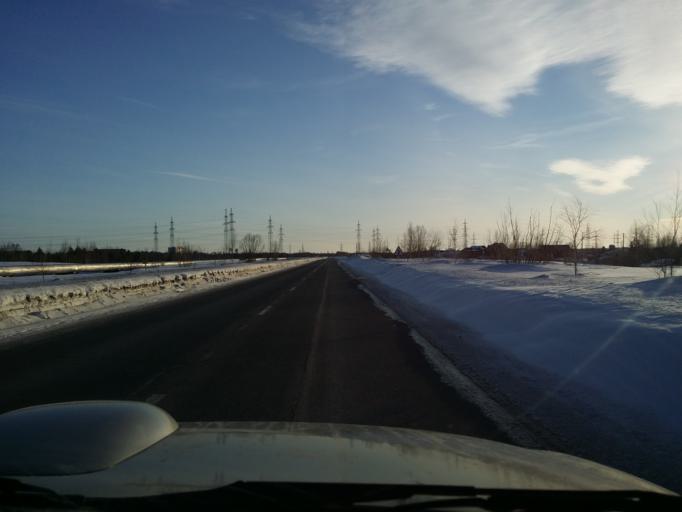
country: RU
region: Khanty-Mansiyskiy Avtonomnyy Okrug
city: Izluchinsk
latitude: 60.9751
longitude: 76.8963
